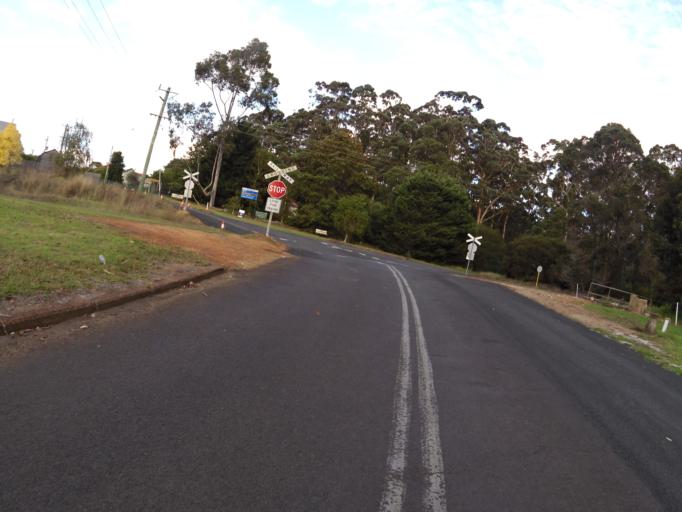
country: AU
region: Western Australia
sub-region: Manjimup
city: Pemberton
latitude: -34.4483
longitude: 116.0317
